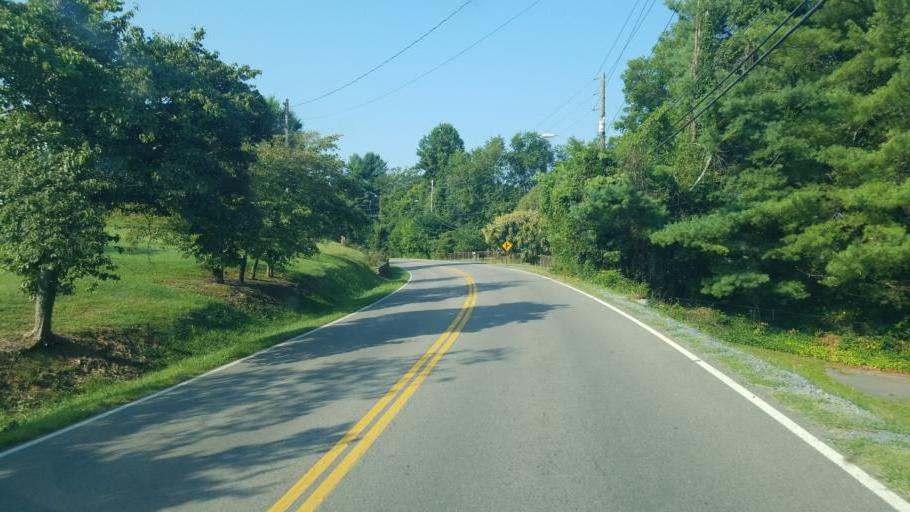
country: US
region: Tennessee
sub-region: Sullivan County
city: Bluff City
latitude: 36.4691
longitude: -82.2746
